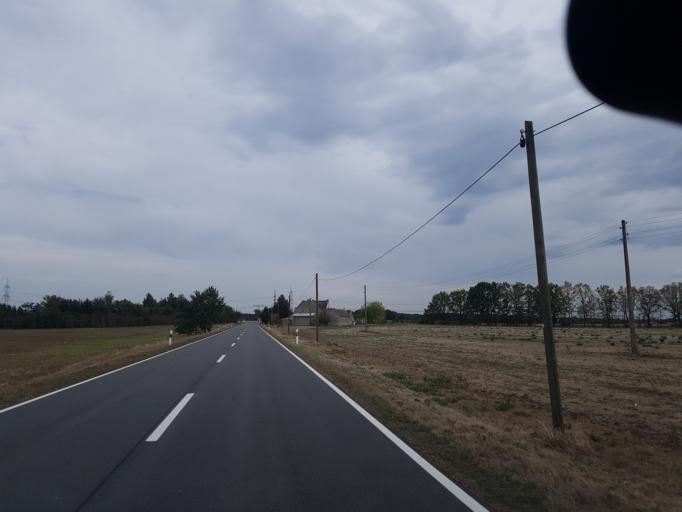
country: DE
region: Saxony-Anhalt
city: Annaburg
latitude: 51.7856
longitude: 13.0264
